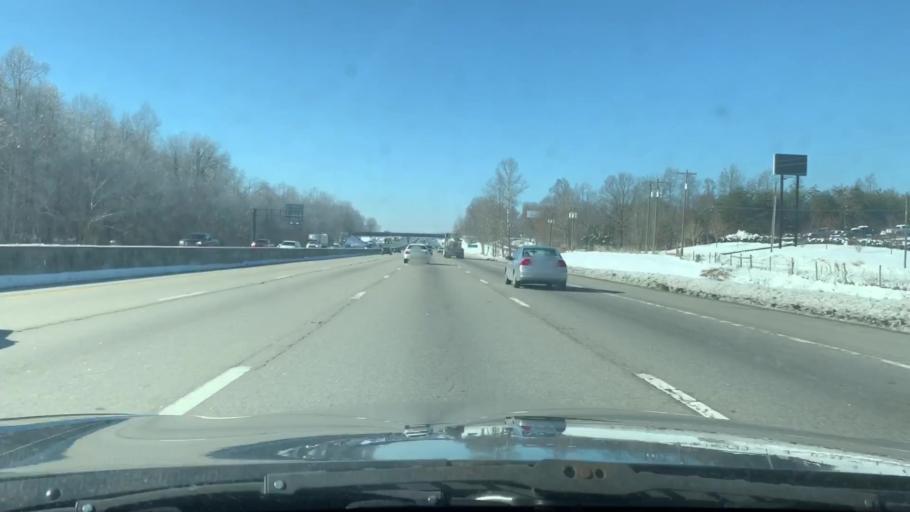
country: US
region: North Carolina
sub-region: Alamance County
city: Mebane
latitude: 36.0783
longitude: -79.2388
